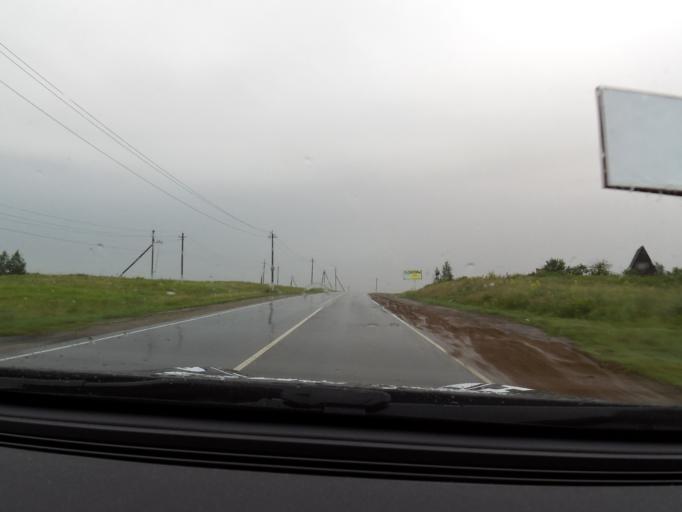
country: RU
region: Tatarstan
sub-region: Tukayevskiy Rayon
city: Naberezhnyye Chelny
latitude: 55.6732
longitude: 52.5165
